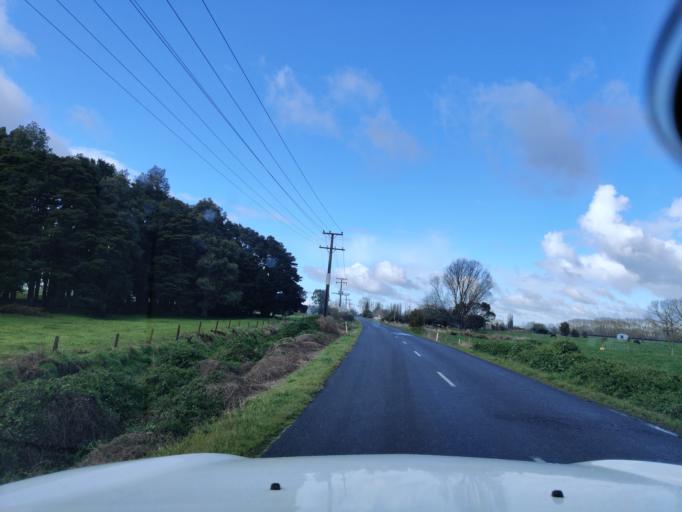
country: NZ
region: Waikato
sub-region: Waikato District
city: Ngaruawahia
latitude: -37.5703
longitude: 175.2643
